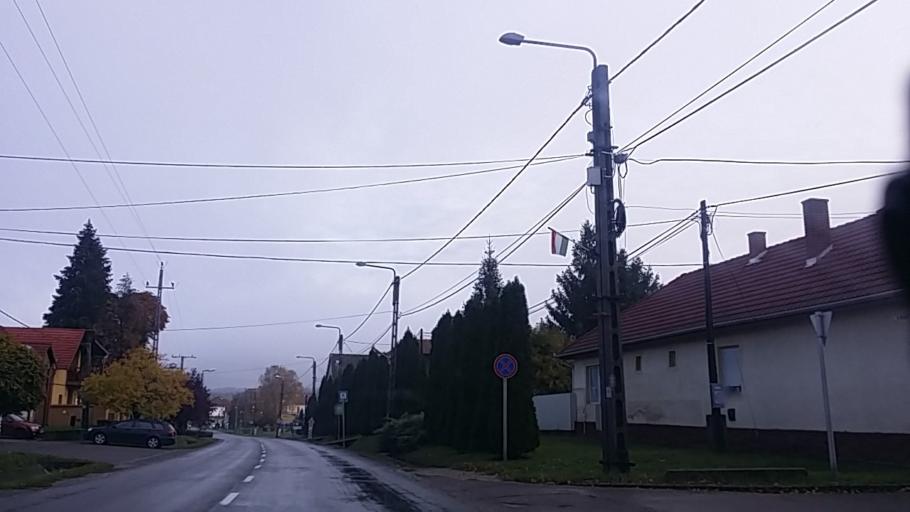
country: HU
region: Heves
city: Belapatfalva
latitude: 48.0558
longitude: 20.3512
